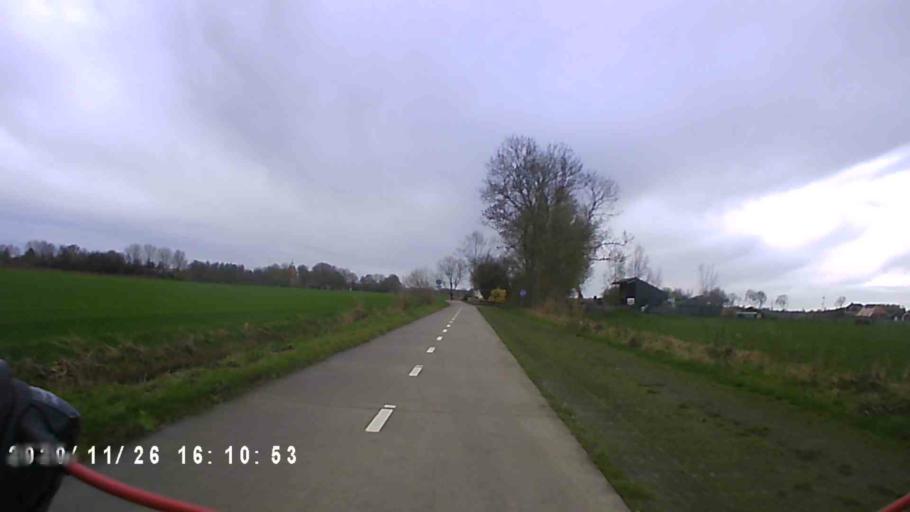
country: NL
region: Groningen
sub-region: Gemeente Bedum
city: Bedum
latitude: 53.2529
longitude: 6.6515
